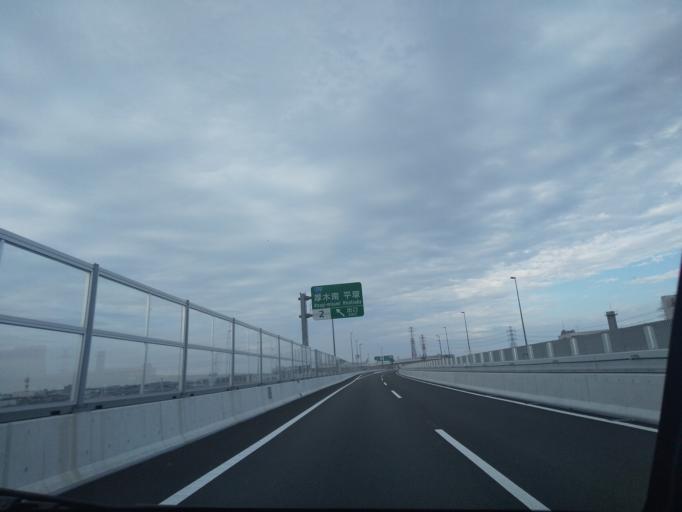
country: JP
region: Kanagawa
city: Atsugi
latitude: 35.4061
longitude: 139.3491
